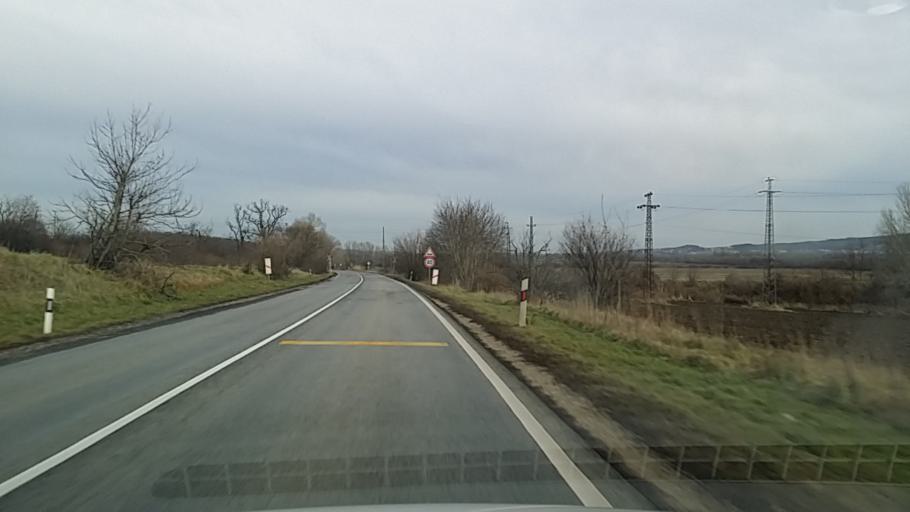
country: HU
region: Fejer
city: Mor
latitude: 47.3581
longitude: 18.2096
